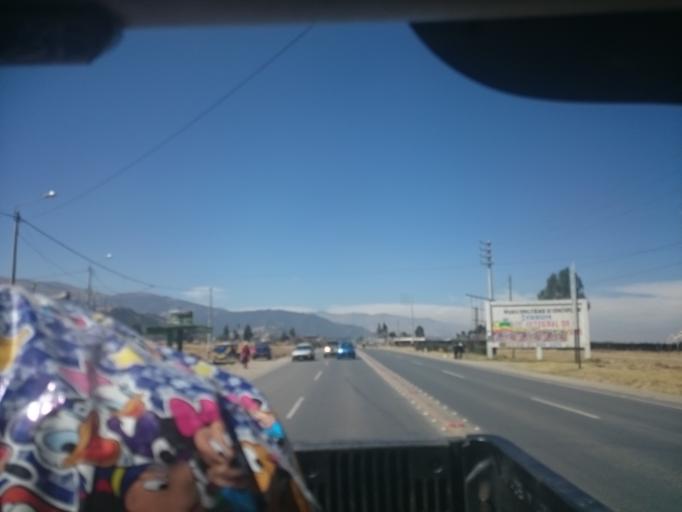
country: PE
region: Junin
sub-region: Provincia de Huancayo
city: San Jeronimo
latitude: -11.9440
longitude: -75.2955
